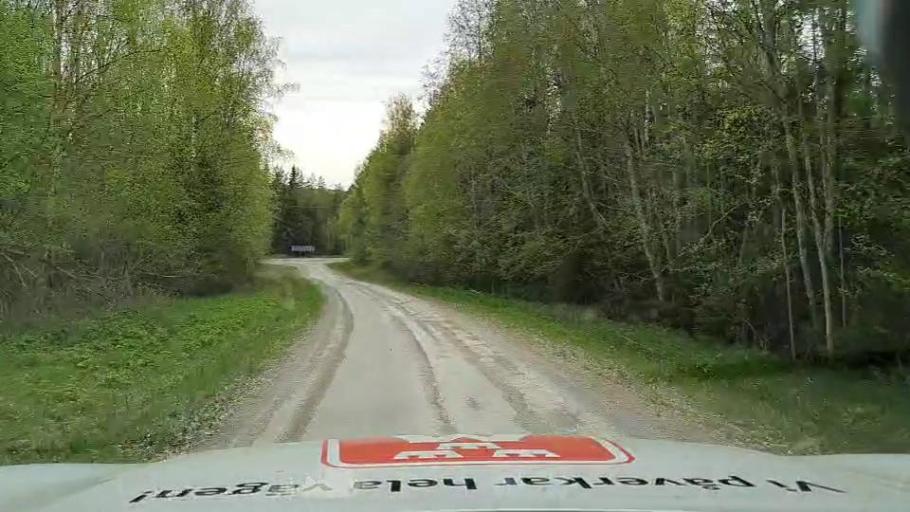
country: SE
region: Jaemtland
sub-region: Bergs Kommun
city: Hoverberg
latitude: 62.6798
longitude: 14.7505
